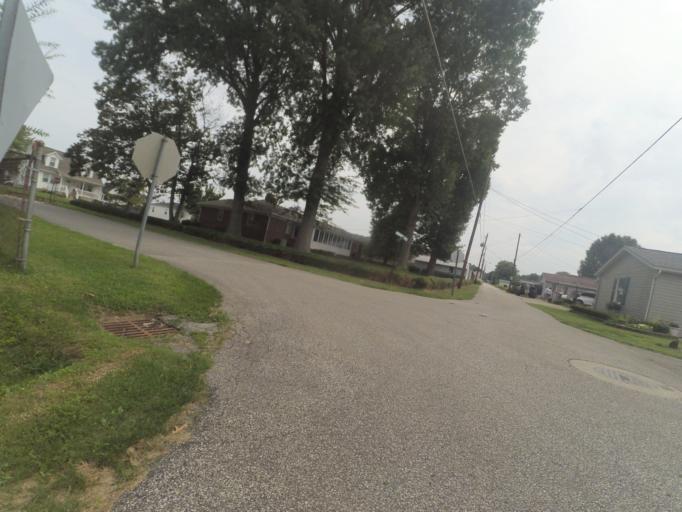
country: US
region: West Virginia
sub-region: Cabell County
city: Huntington
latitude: 38.4261
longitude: -82.4591
